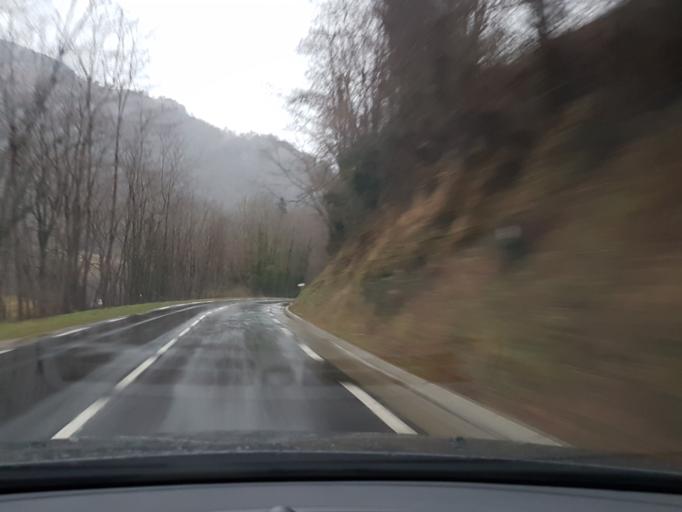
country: FR
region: Midi-Pyrenees
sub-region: Departement de l'Ariege
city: Saint-Girons
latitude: 42.9313
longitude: 1.1786
